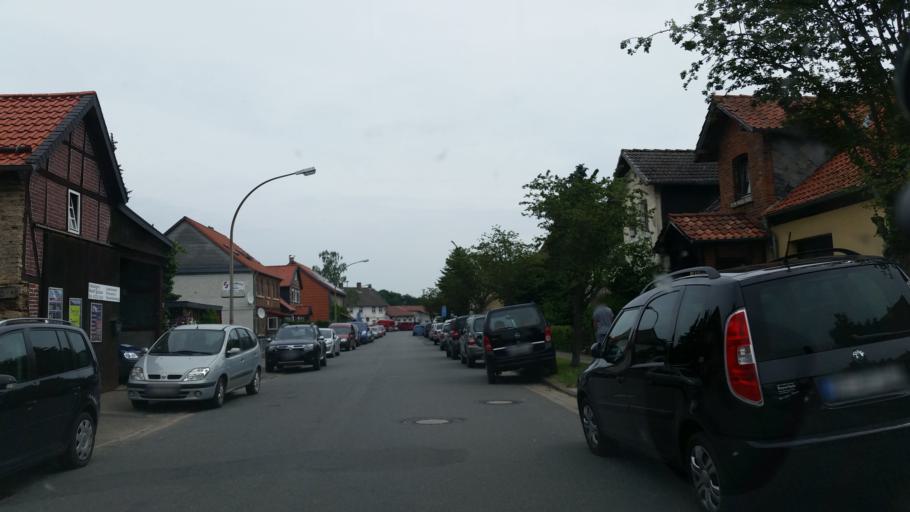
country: DE
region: Lower Saxony
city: Konigslutter am Elm
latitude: 52.2963
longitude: 10.7880
